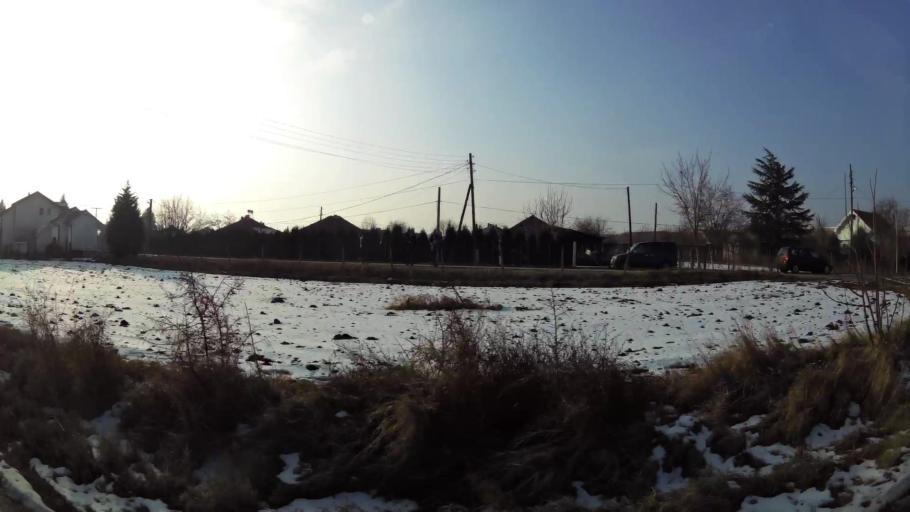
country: MK
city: Miladinovci
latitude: 41.9823
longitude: 21.6503
